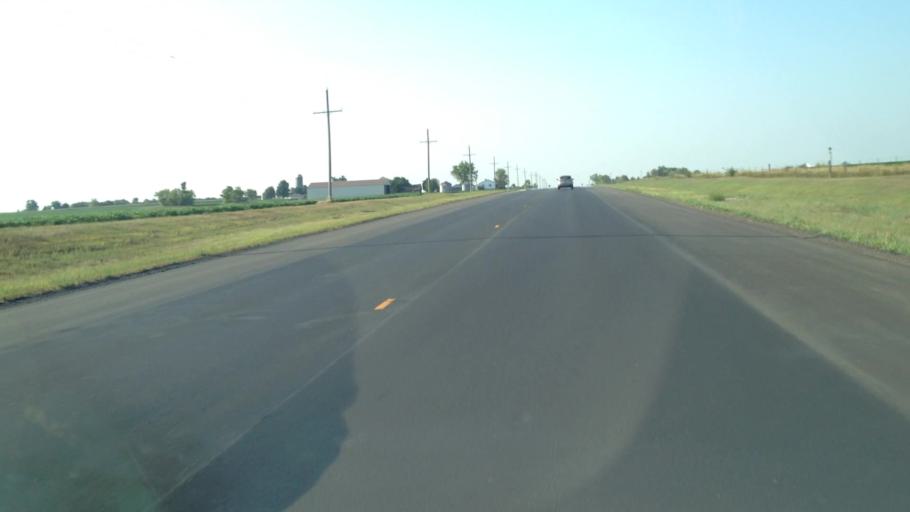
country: US
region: Kansas
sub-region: Franklin County
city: Ottawa
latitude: 38.5003
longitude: -95.2675
